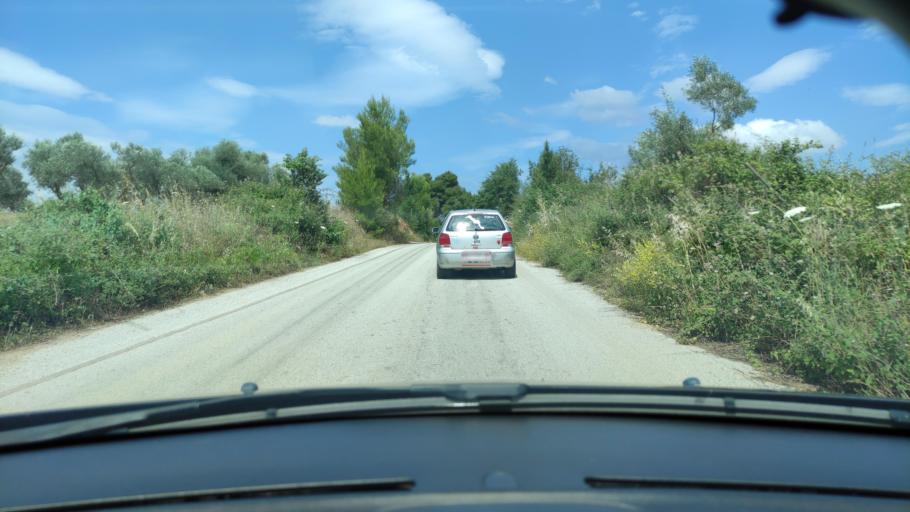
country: GR
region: Central Greece
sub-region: Nomos Evvoias
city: Afration
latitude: 38.5189
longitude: 23.7609
